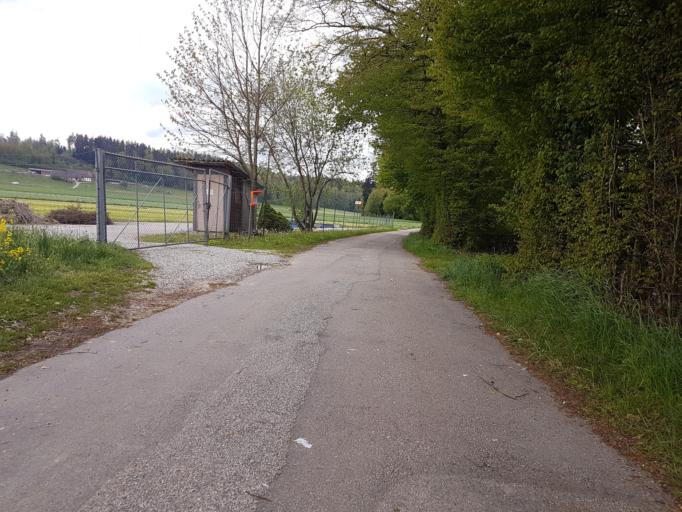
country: CH
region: Bern
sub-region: Oberaargau
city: Aarwangen
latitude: 47.2407
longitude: 7.7538
